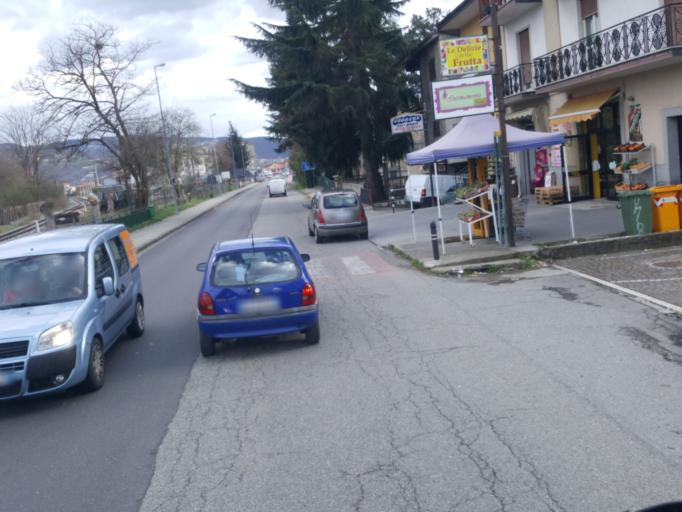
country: IT
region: Calabria
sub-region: Provincia di Cosenza
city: Santo Stefano di Rogliano
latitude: 39.2020
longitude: 16.3128
